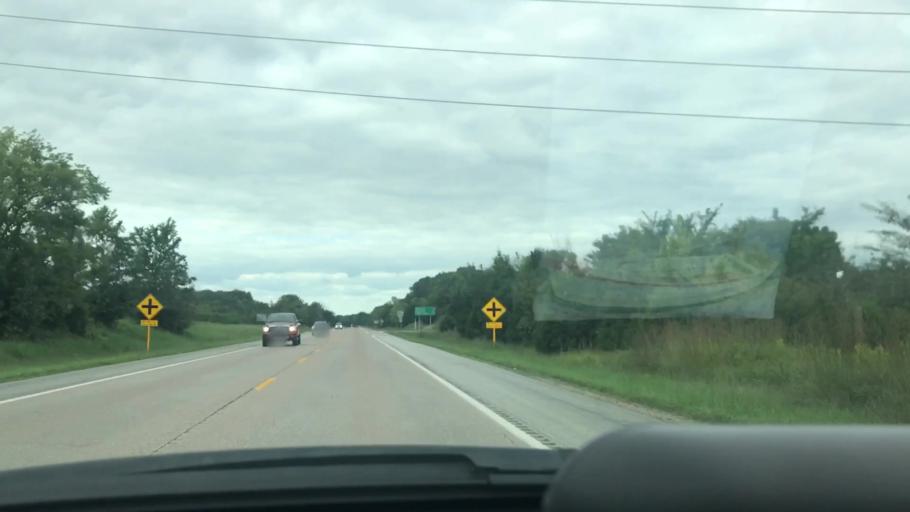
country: US
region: Missouri
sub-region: Benton County
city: Warsaw
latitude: 38.1941
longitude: -93.3246
